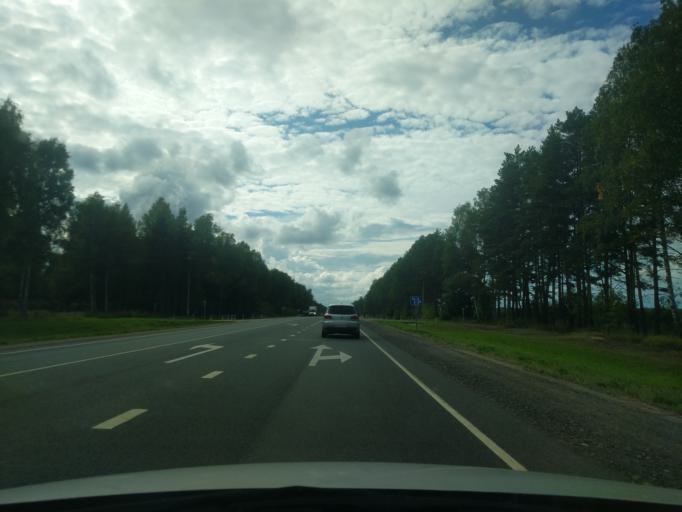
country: RU
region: Jaroslavl
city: Levashevo
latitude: 57.6421
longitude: 40.4912
